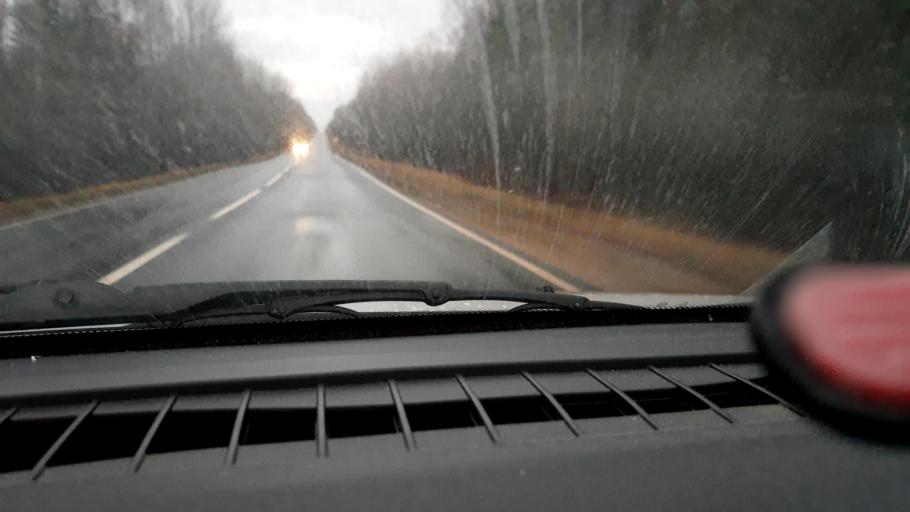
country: RU
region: Nizjnij Novgorod
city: Uren'
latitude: 57.2659
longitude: 45.6209
